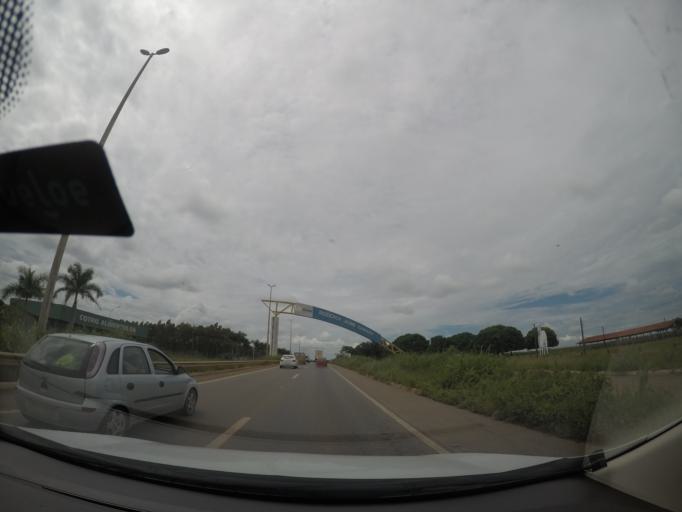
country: BR
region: Goias
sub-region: Inhumas
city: Inhumas
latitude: -16.3949
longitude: -49.4936
